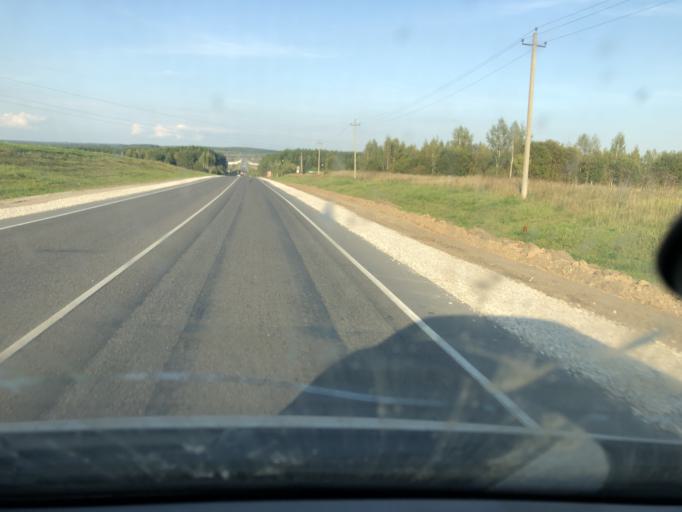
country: RU
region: Kaluga
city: Peremyshl'
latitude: 54.2800
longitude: 36.1472
